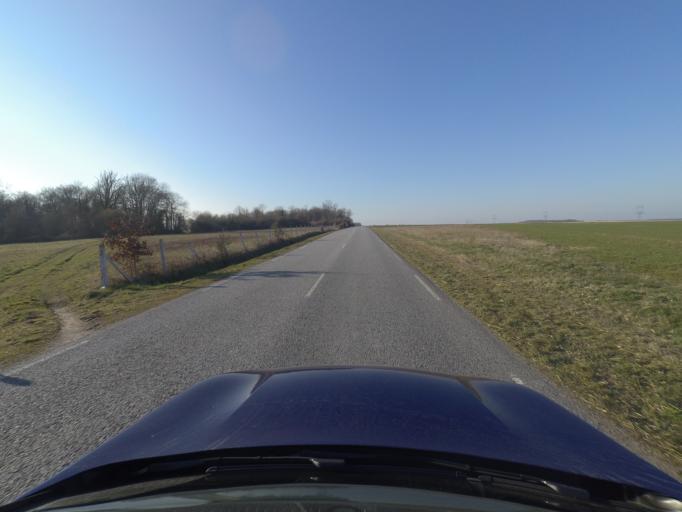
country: FR
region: Haute-Normandie
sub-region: Departement de l'Eure
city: Damville
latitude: 48.8952
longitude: 1.0388
